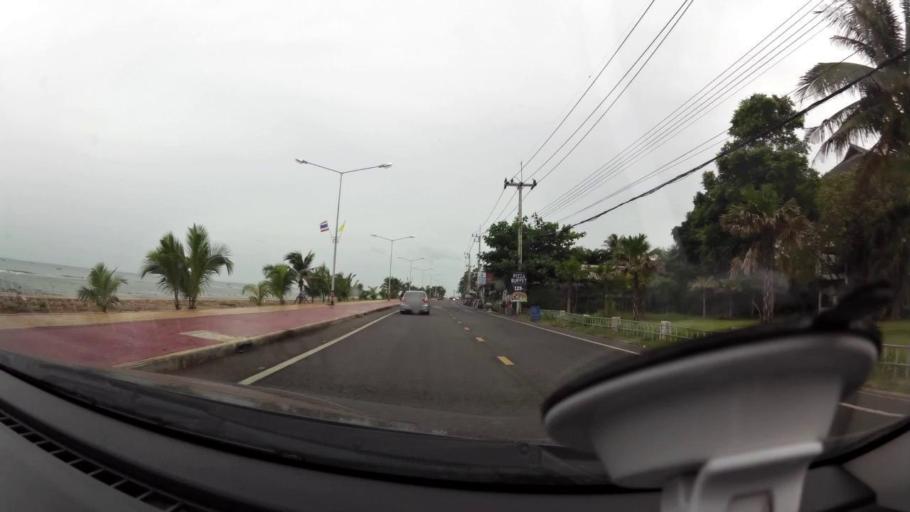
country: TH
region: Prachuap Khiri Khan
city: Pran Buri
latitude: 12.3811
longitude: 99.9998
